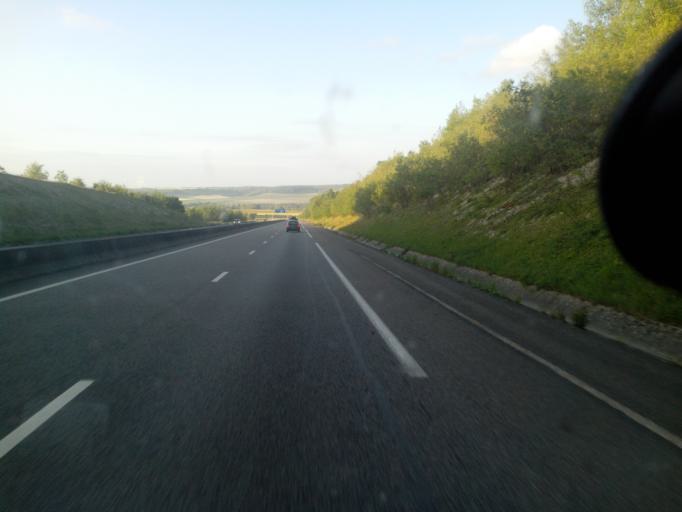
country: FR
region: Haute-Normandie
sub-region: Departement de la Seine-Maritime
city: Neufchatel-en-Bray
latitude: 49.7495
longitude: 1.4796
